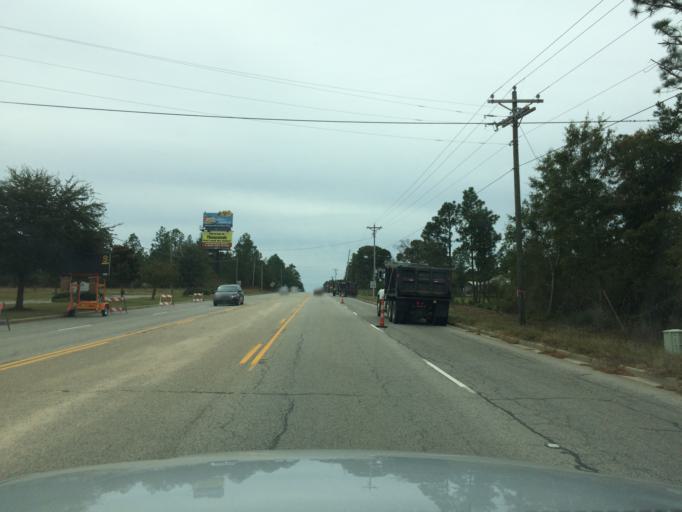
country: US
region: South Carolina
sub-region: Aiken County
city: Aiken
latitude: 33.5980
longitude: -81.6888
